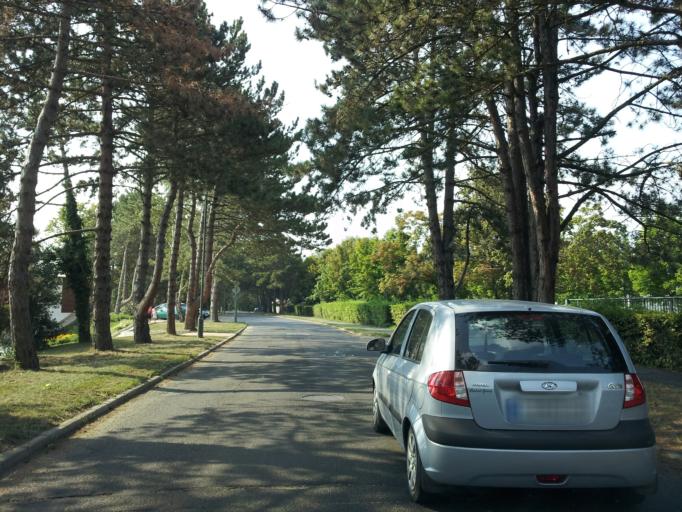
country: HU
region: Vas
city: Szombathely
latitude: 47.2357
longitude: 16.6007
